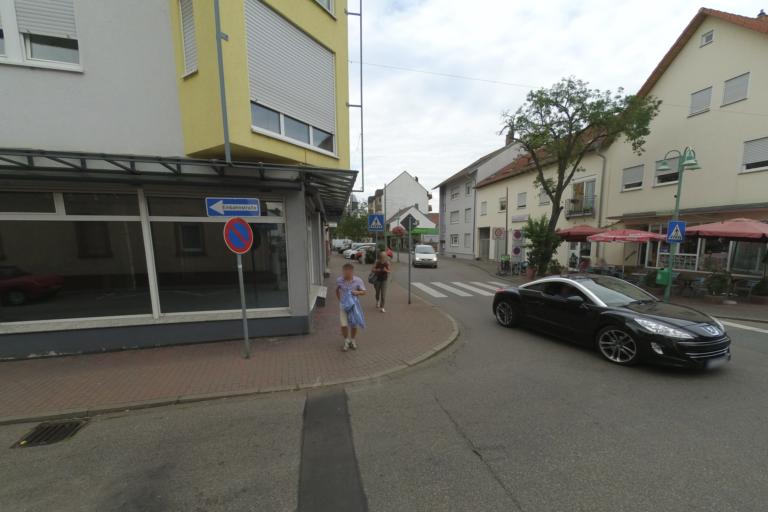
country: DE
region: Hesse
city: Viernheim
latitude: 49.5351
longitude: 8.5761
